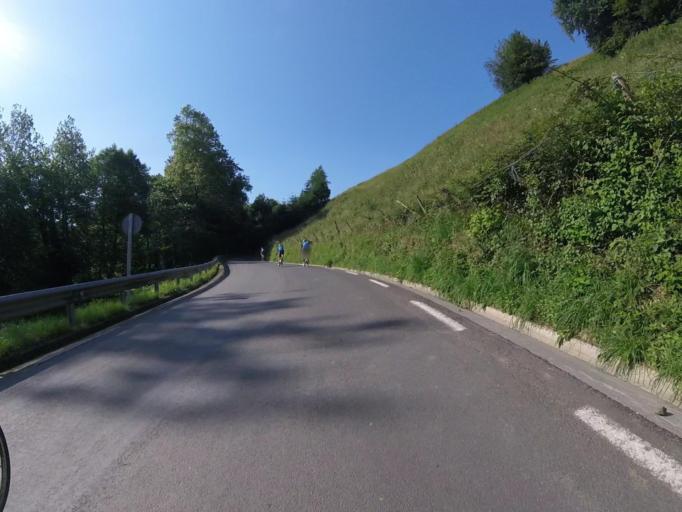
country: ES
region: Basque Country
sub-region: Provincia de Guipuzcoa
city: Zizurkil
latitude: 43.1881
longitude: -2.0826
